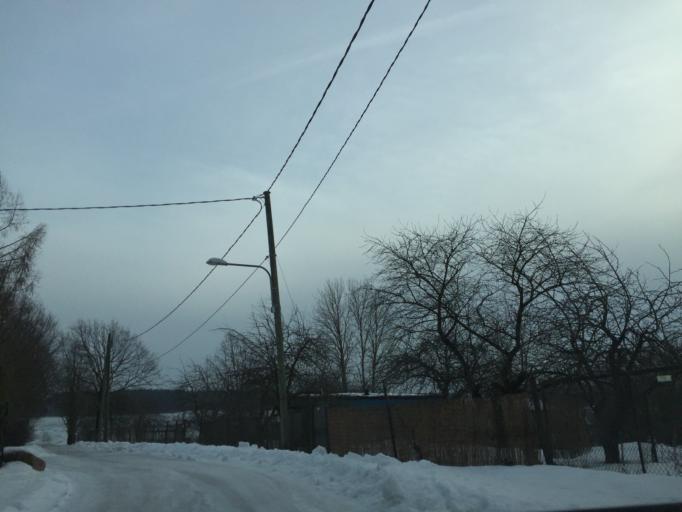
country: LV
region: Salaspils
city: Salaspils
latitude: 56.8428
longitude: 24.4313
